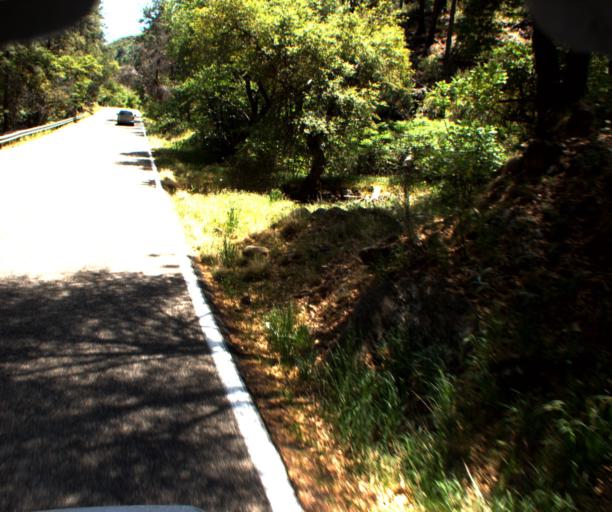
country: US
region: Arizona
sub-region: Coconino County
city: Sedona
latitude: 34.9338
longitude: -111.7423
